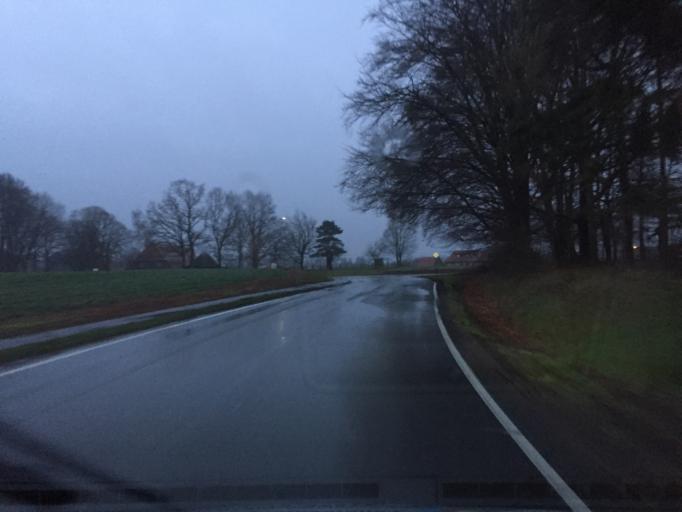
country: DE
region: Lower Saxony
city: Sudwalde
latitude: 52.8433
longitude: 8.8458
